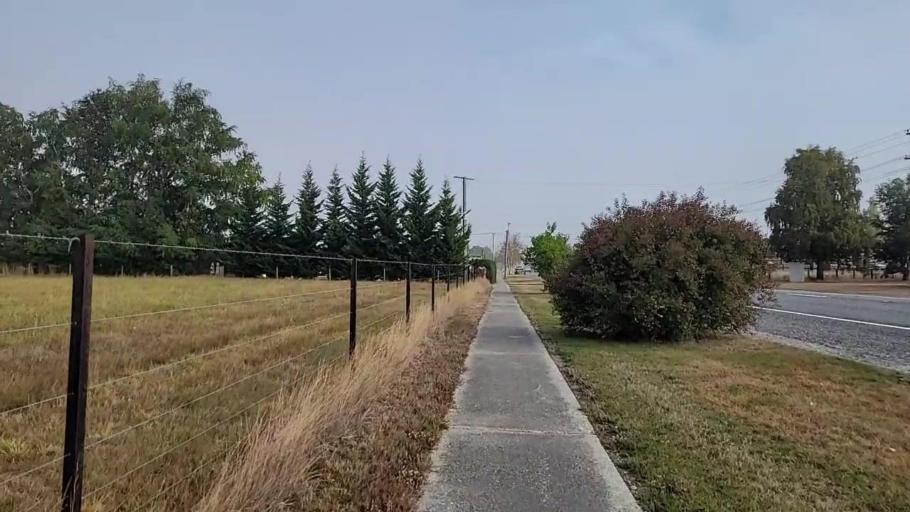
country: NZ
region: Southland
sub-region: Gore District
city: Gore
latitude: -45.6380
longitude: 169.3686
